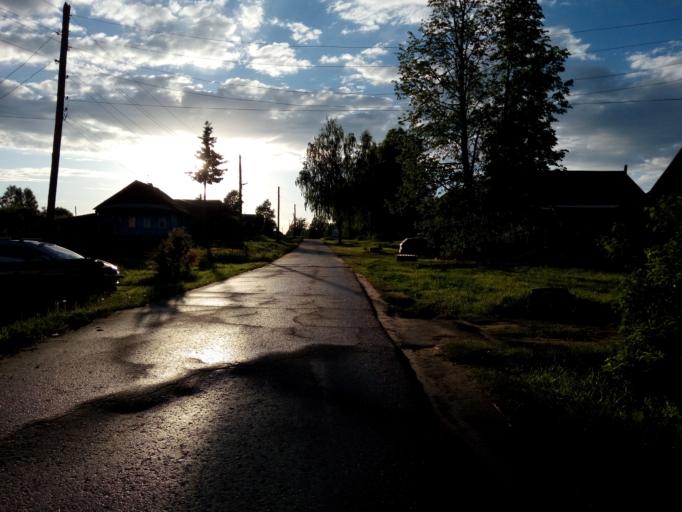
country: RU
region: Nizjnij Novgorod
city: Voskresenskoye
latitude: 56.7735
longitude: 45.5514
